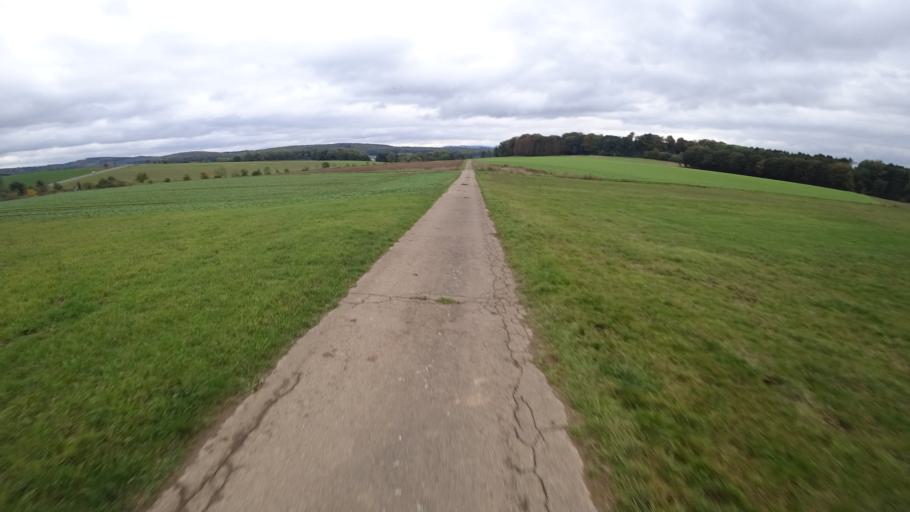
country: DE
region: Rheinland-Pfalz
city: Maxsain
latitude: 50.5596
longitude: 7.7781
